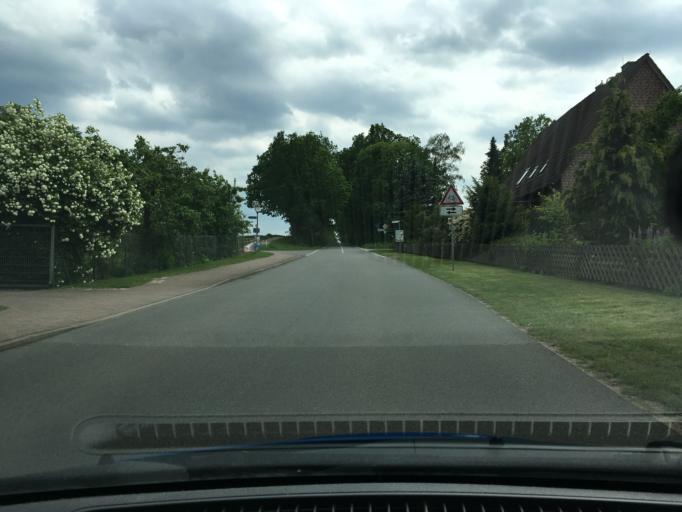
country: DE
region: Lower Saxony
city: Betzendorf
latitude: 53.1355
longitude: 10.3101
